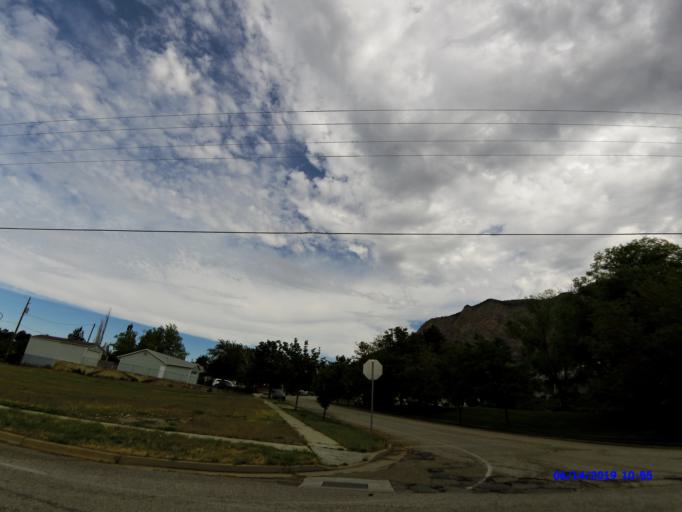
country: US
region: Utah
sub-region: Weber County
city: Ogden
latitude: 41.2484
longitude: -111.9420
